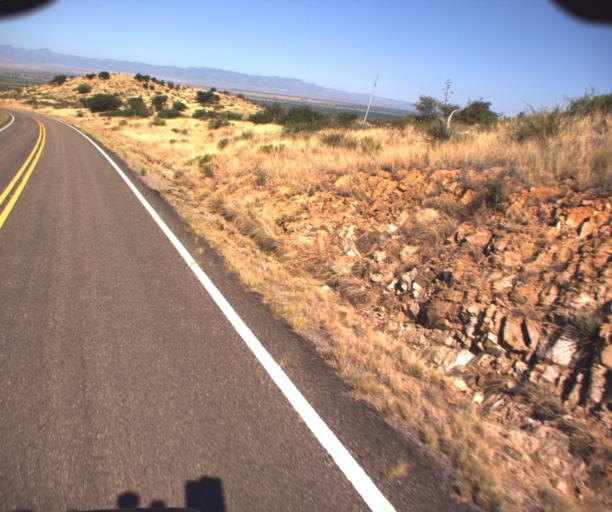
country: US
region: Arizona
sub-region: Graham County
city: Swift Trail Junction
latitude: 32.6002
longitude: -109.8891
